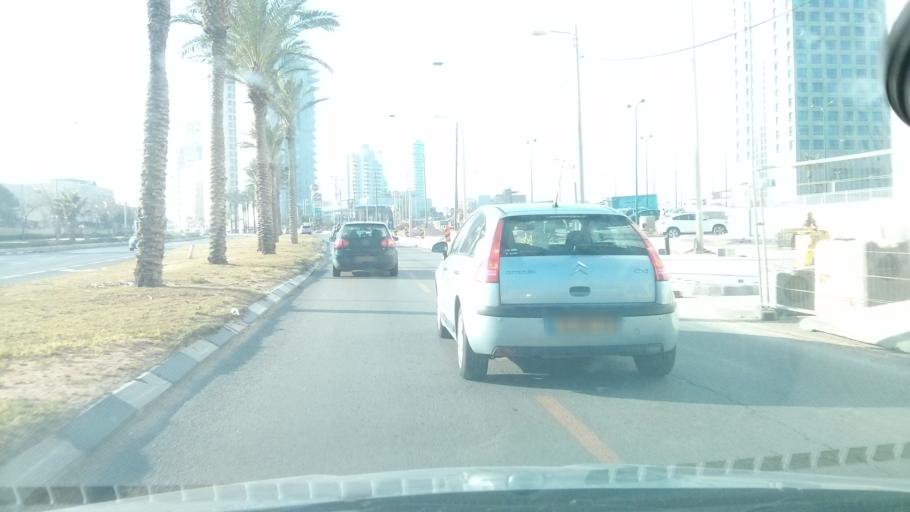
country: IL
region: Central District
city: Netanya
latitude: 32.3194
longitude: 34.8480
